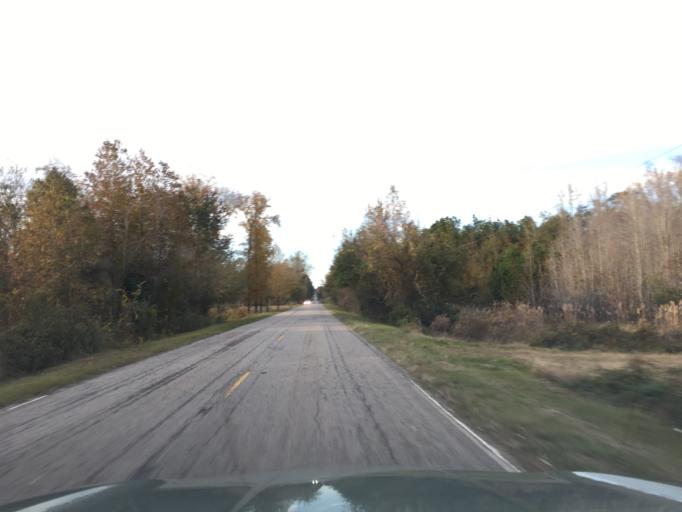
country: US
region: South Carolina
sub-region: Lexington County
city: Red Bank
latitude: 33.7242
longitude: -81.3577
